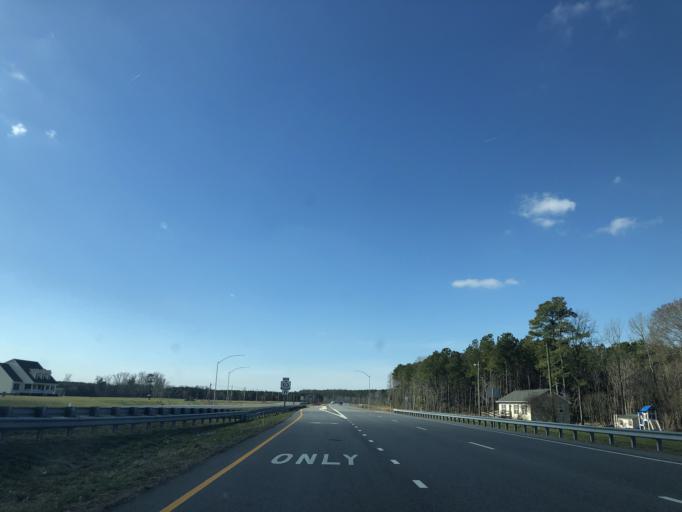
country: US
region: Maryland
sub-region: Worcester County
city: Snow Hill
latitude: 38.2349
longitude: -75.3236
